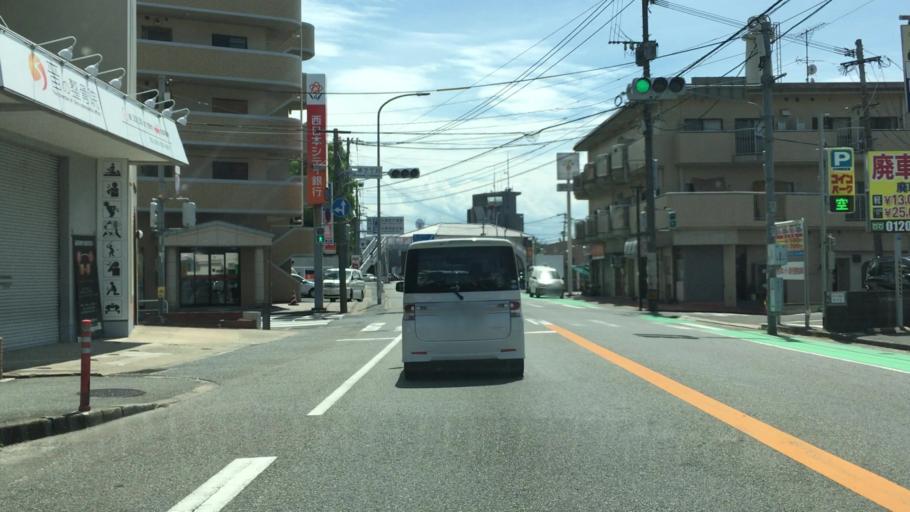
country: JP
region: Fukuoka
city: Dazaifu
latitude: 33.5141
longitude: 130.5069
